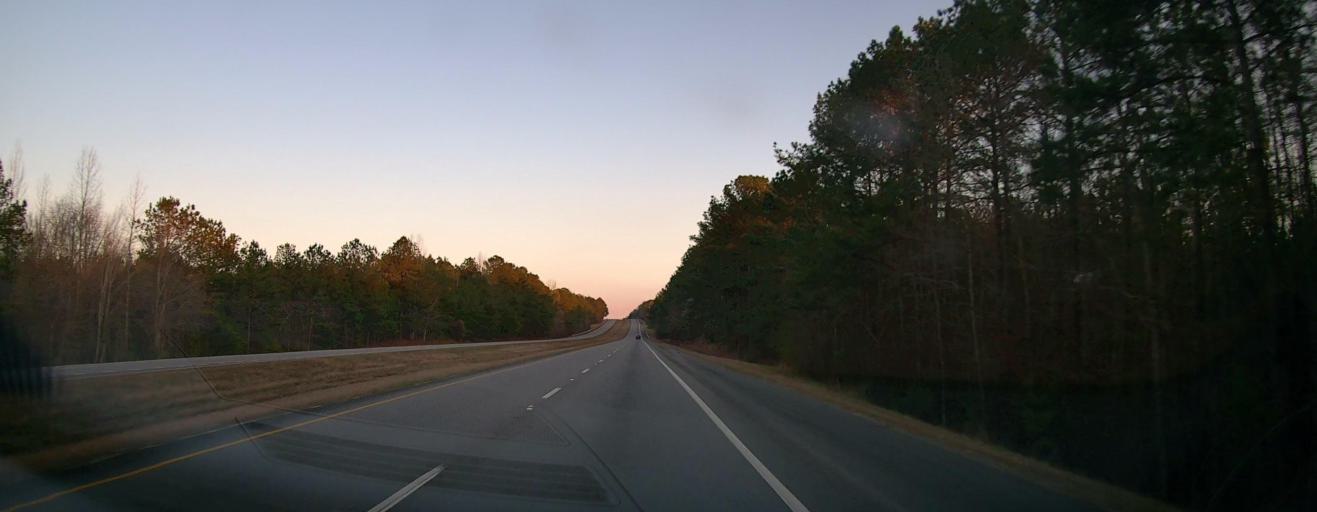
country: US
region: Alabama
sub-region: Coosa County
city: Goodwater
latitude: 33.0275
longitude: -86.1118
